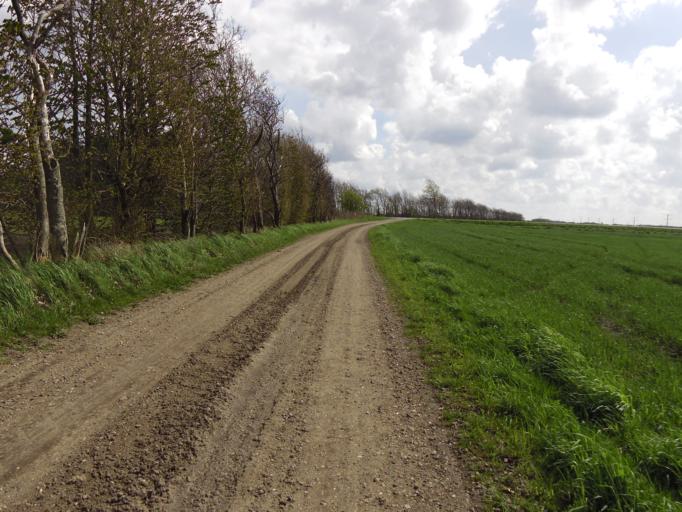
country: DK
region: South Denmark
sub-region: Tonder Kommune
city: Toftlund
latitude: 55.2044
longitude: 9.1565
